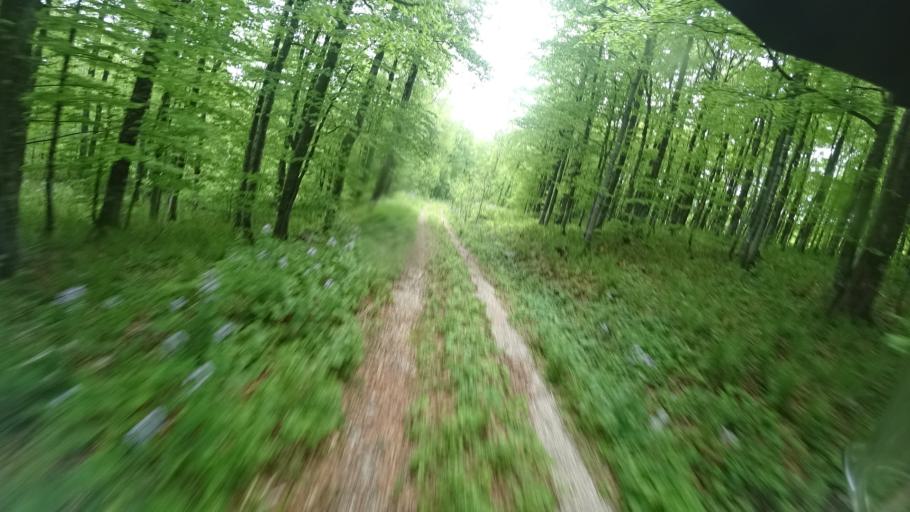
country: BA
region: Federation of Bosnia and Herzegovina
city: Orasac
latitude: 44.5680
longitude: 15.8802
